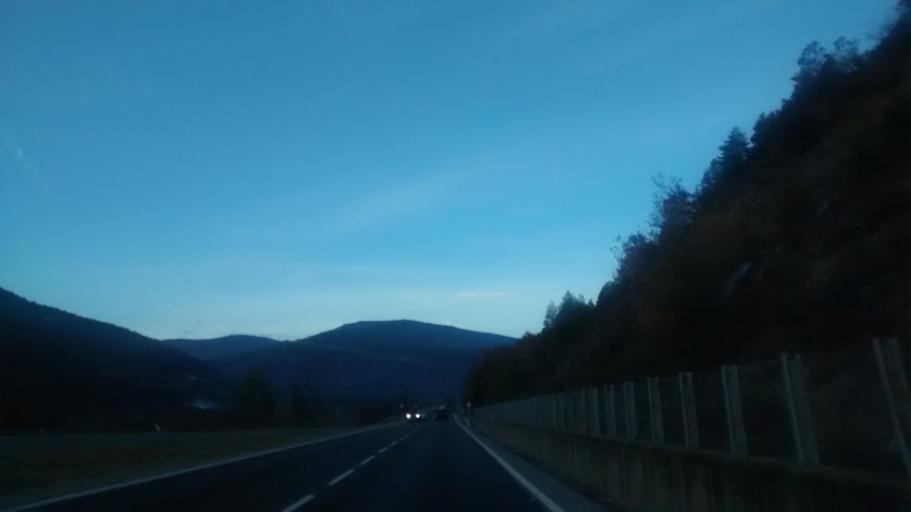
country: ES
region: Catalonia
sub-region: Provincia de Lleida
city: Coll de Nargo
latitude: 42.2724
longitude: 1.3607
